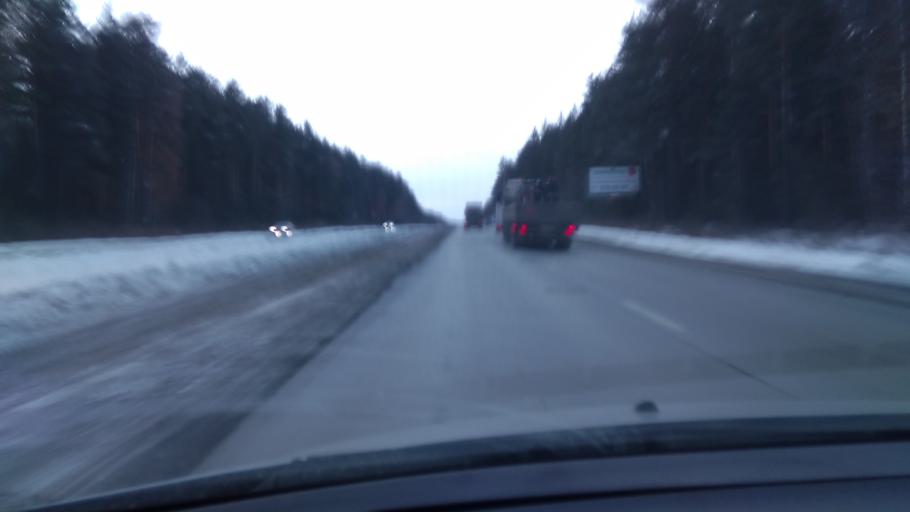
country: RU
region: Sverdlovsk
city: Sysert'
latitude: 56.5773
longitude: 60.8574
